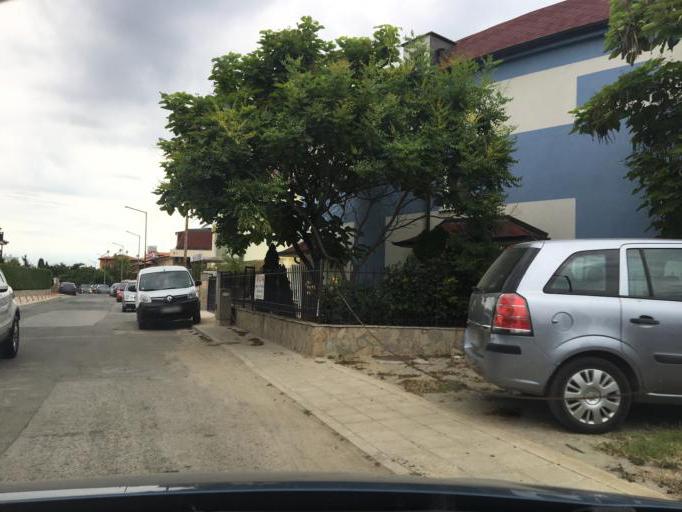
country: BG
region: Burgas
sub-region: Obshtina Sozopol
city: Sozopol
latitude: 42.4069
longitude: 27.7098
